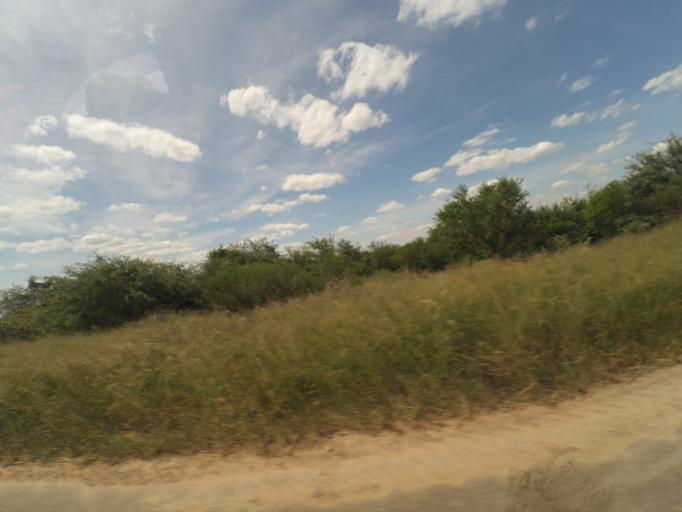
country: BO
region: Santa Cruz
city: Pailon
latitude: -17.5895
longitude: -61.9710
